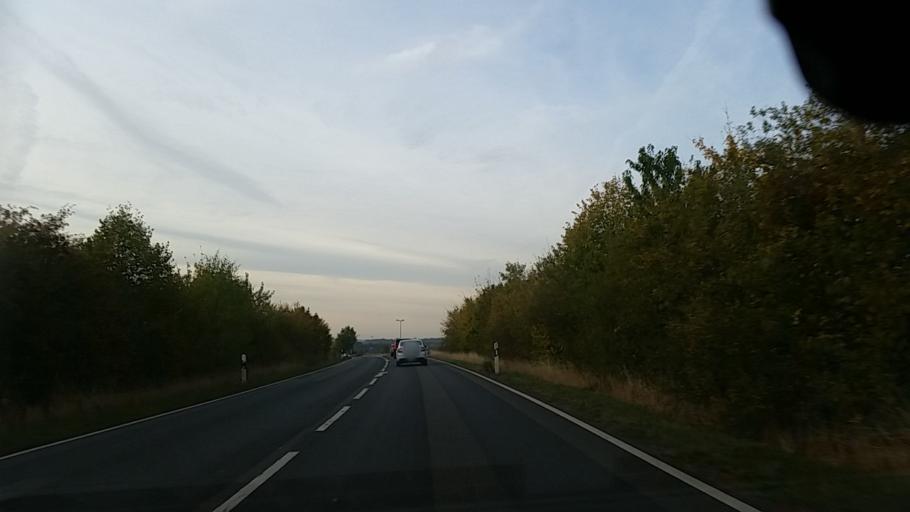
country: DE
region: Lower Saxony
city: Wolfsburg
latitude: 52.4463
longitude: 10.8259
